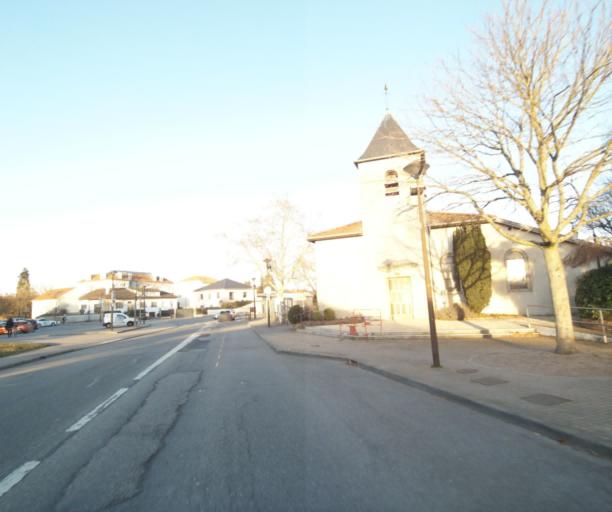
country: FR
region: Lorraine
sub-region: Departement de Meurthe-et-Moselle
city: Pulnoy
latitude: 48.7019
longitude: 6.2577
